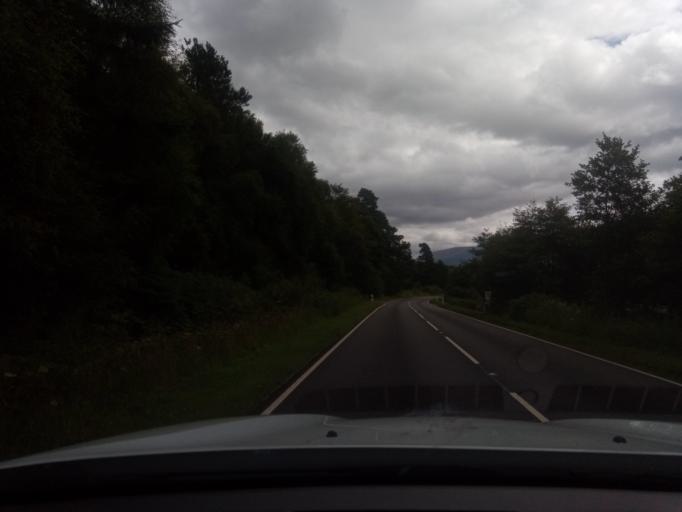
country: GB
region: Scotland
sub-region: Highland
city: Fort William
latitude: 56.8557
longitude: -5.1937
